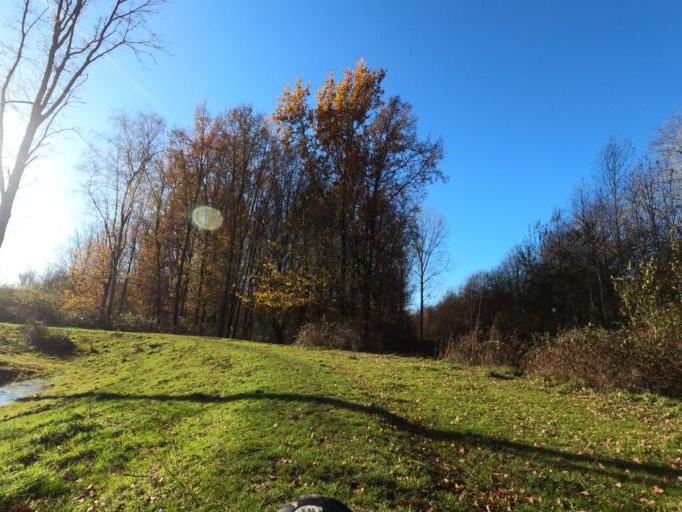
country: NL
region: Gelderland
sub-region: Gemeente Nijkerk
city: Nijkerk
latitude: 52.2696
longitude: 5.4429
